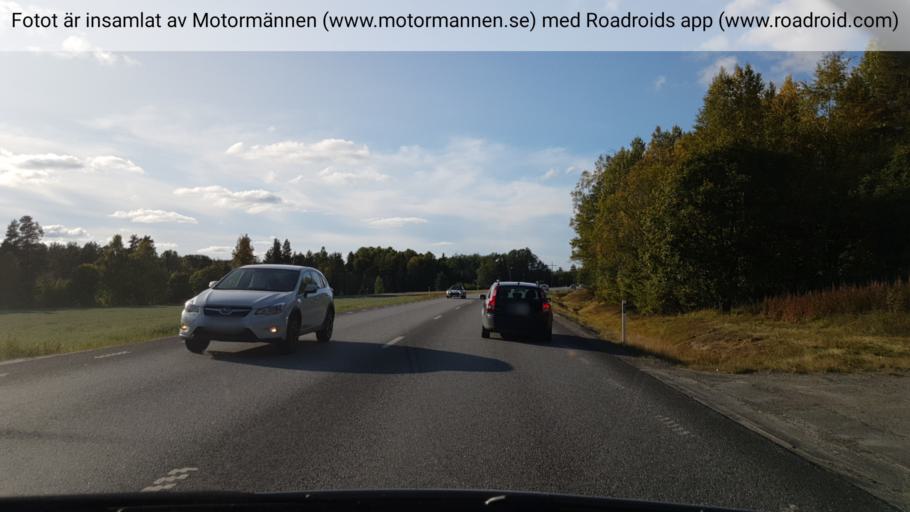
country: SE
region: Vaesterbotten
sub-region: Umea Kommun
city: Roback
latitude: 63.8537
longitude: 20.1025
